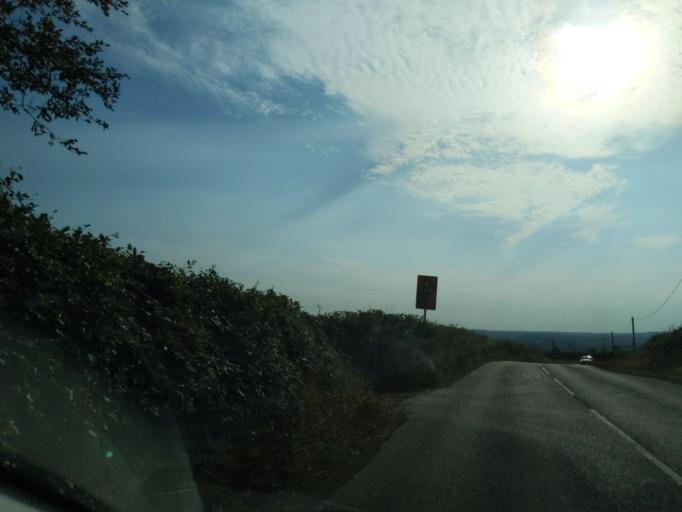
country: GB
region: England
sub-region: Devon
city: Great Torrington
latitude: 50.9624
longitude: -4.0977
